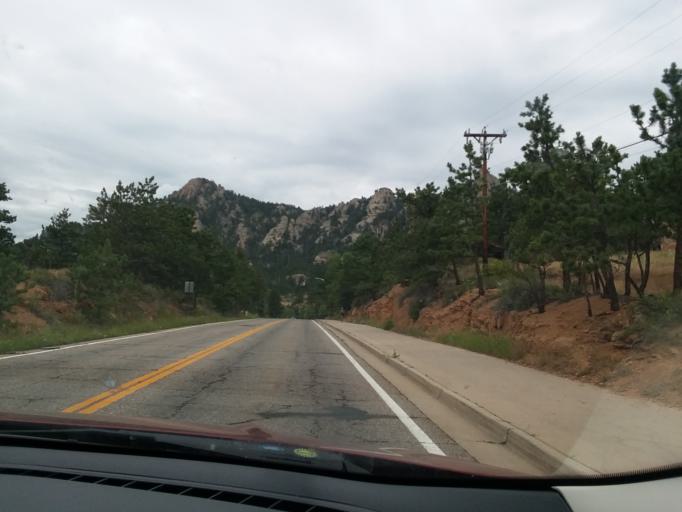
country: US
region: Colorado
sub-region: Larimer County
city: Estes Park
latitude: 40.3802
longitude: -105.5382
